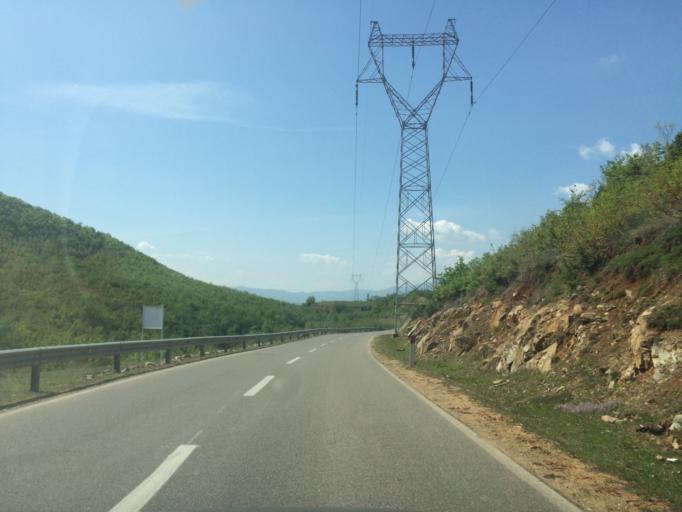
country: AL
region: Kukes
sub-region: Rrethi i Tropojes
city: Llugaj
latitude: 42.3827
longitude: 20.1340
